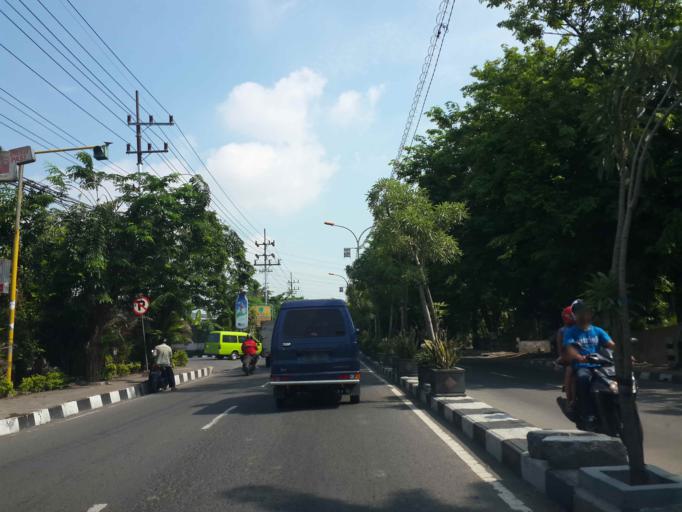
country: ID
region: East Java
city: Kebomas
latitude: -7.1882
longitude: 112.6471
